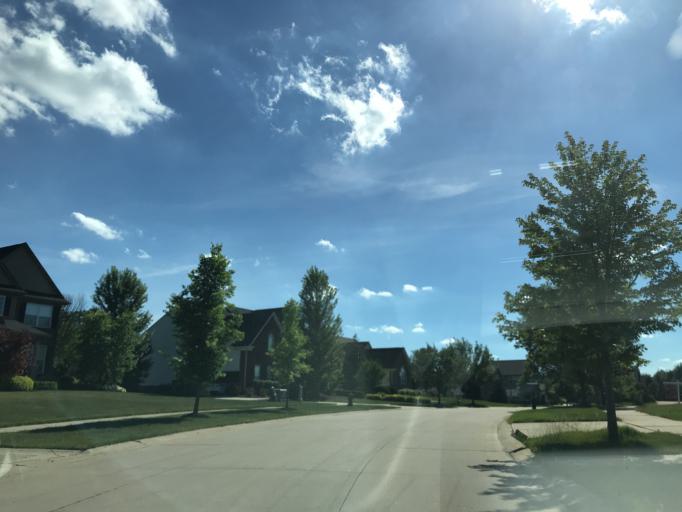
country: US
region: Michigan
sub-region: Oakland County
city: Wixom
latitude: 42.4596
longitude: -83.5670
